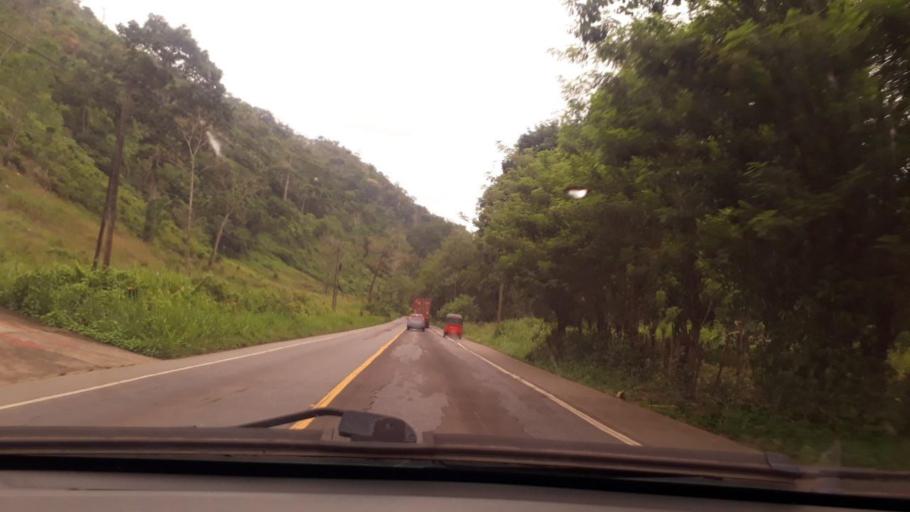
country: GT
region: Izabal
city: Morales
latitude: 15.5438
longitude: -88.7144
